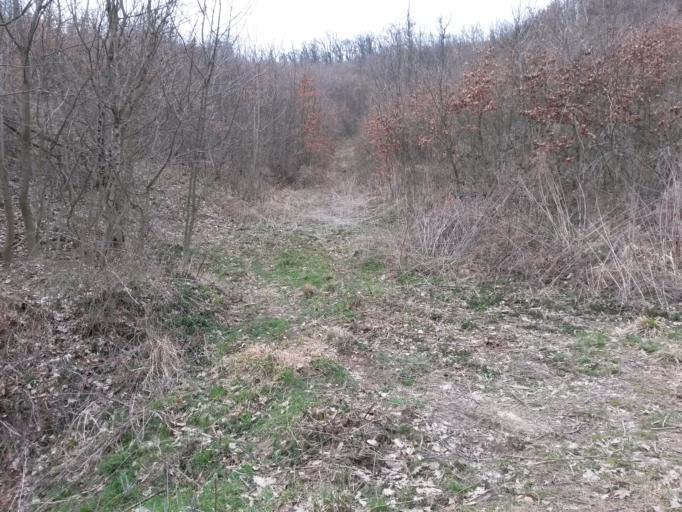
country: HU
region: Pest
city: Piliscsaba
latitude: 47.5919
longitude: 18.8261
